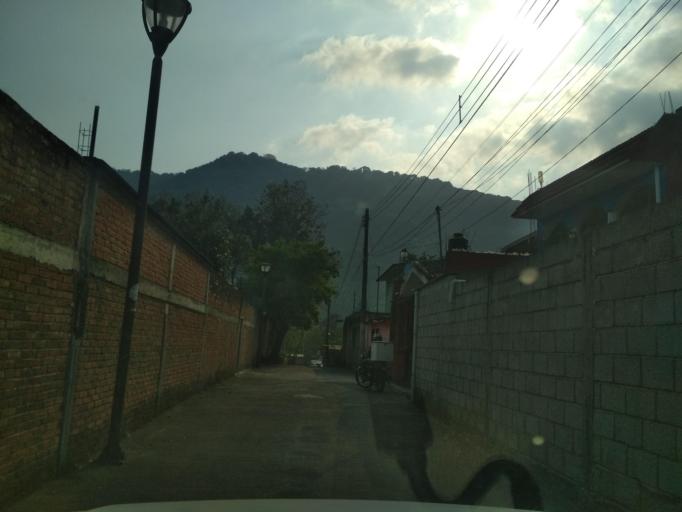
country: MX
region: Veracruz
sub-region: Ixhuatlancillo
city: Fraccionamiento Valle Dorado
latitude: 18.8667
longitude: -97.1180
